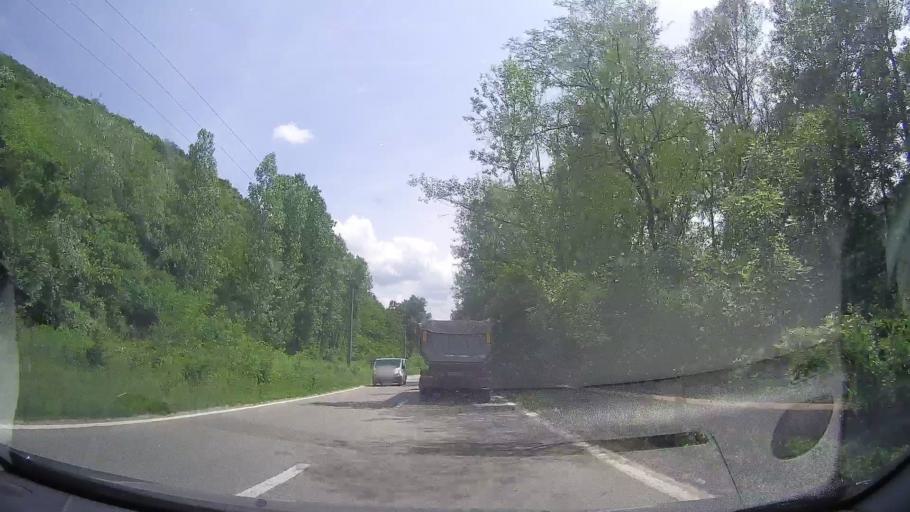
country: RO
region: Valcea
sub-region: Oras Calimanesti
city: Calimanesti
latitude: 45.2756
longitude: 24.3154
